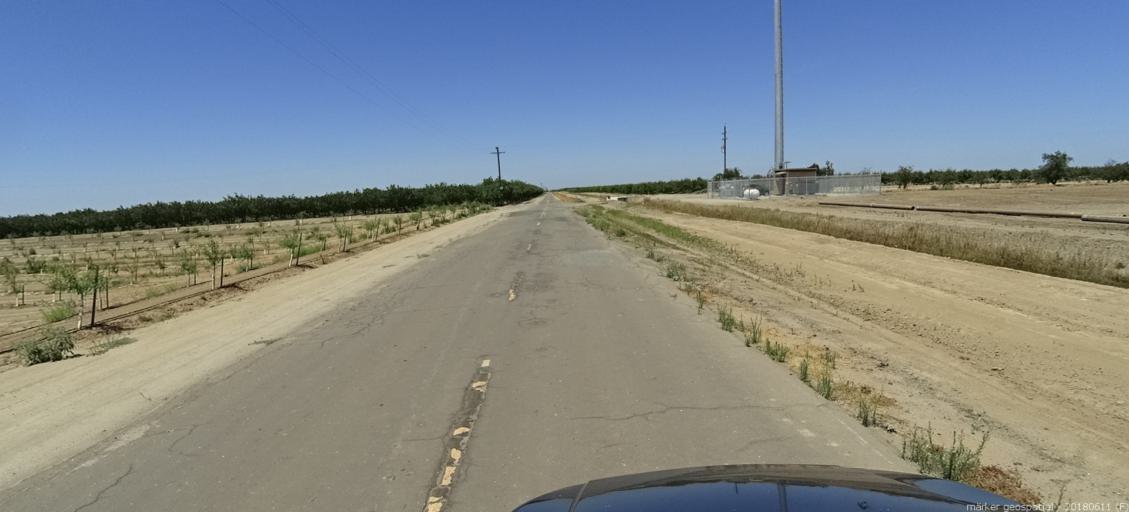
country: US
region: California
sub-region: Madera County
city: Fairmead
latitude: 37.0256
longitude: -120.2104
